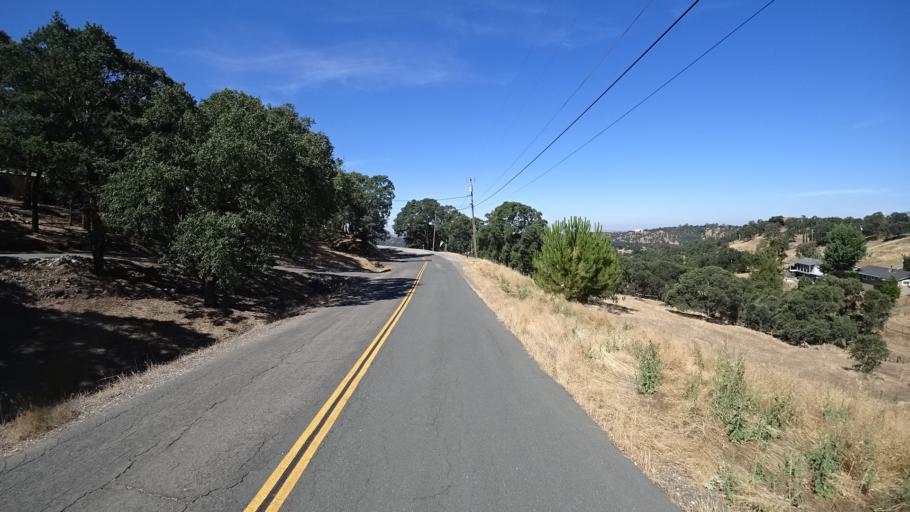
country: US
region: California
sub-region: Calaveras County
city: Rancho Calaveras
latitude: 38.1467
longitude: -120.8493
